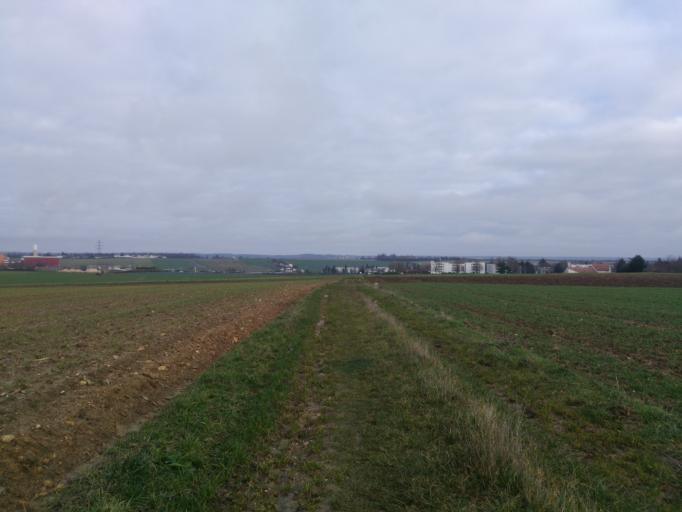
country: FR
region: Ile-de-France
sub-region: Departement des Yvelines
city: Plaisir
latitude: 48.8258
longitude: 1.9303
